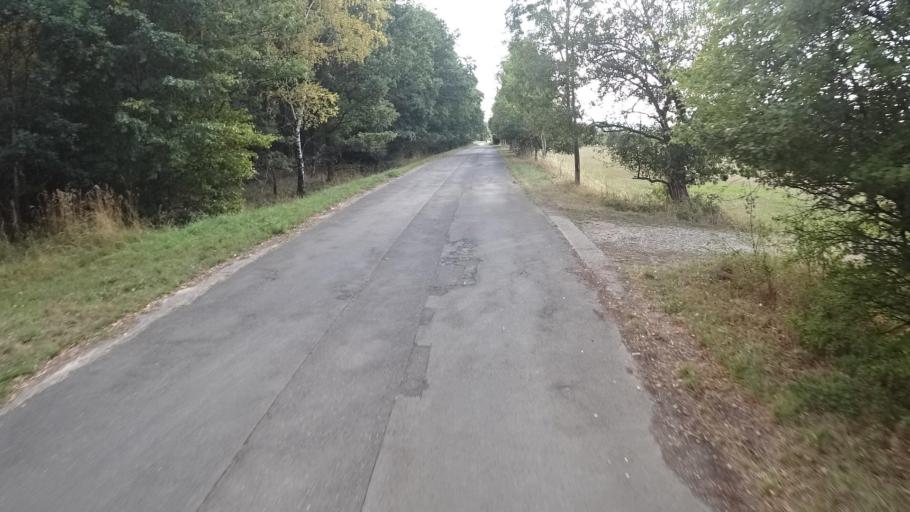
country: DE
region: Rheinland-Pfalz
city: Dichtelbach
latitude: 50.0079
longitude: 7.7061
